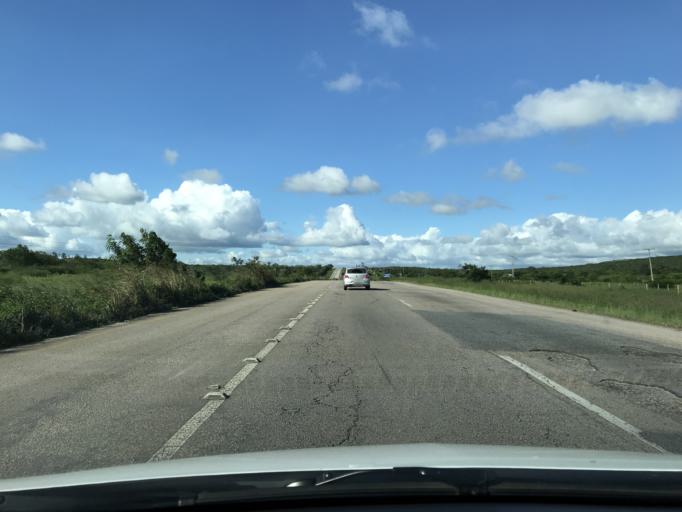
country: BR
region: Pernambuco
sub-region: Bezerros
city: Bezerros
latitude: -8.2278
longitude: -35.6990
